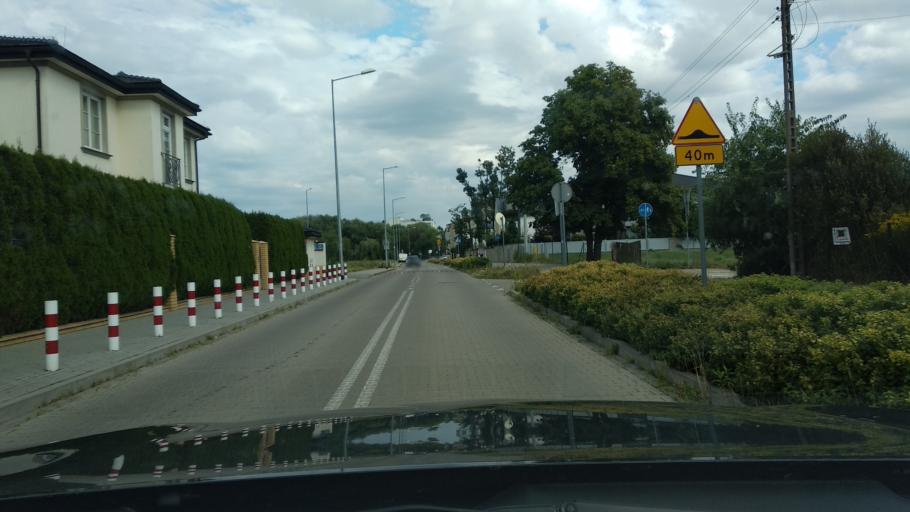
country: PL
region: Masovian Voivodeship
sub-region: Warszawa
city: Ursynow
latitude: 52.1320
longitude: 21.0497
